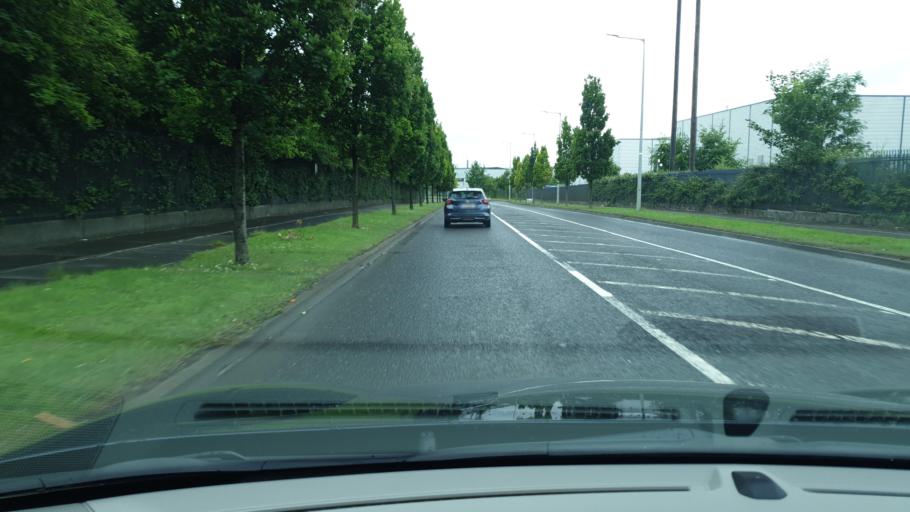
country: IE
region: Leinster
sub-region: Fingal County
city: Blanchardstown
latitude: 53.4109
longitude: -6.3447
